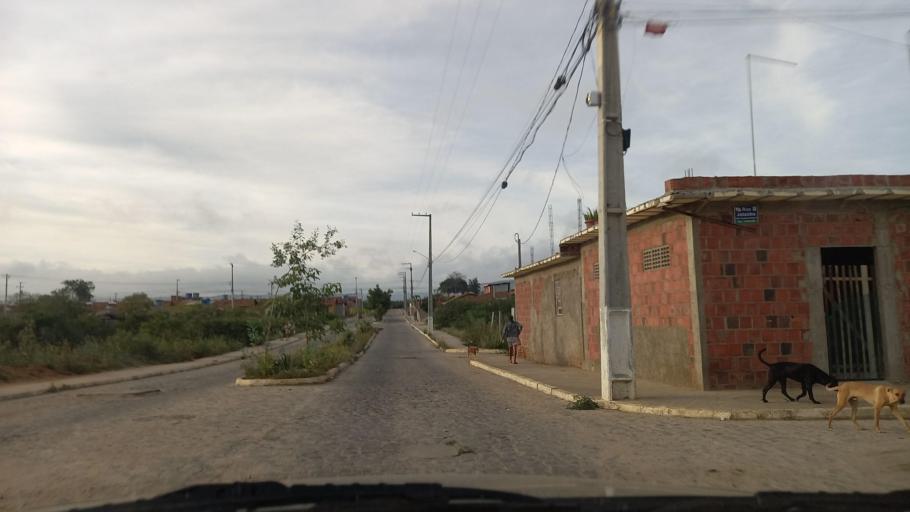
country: BR
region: Pernambuco
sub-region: Bezerros
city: Bezerros
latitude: -8.2163
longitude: -35.7403
